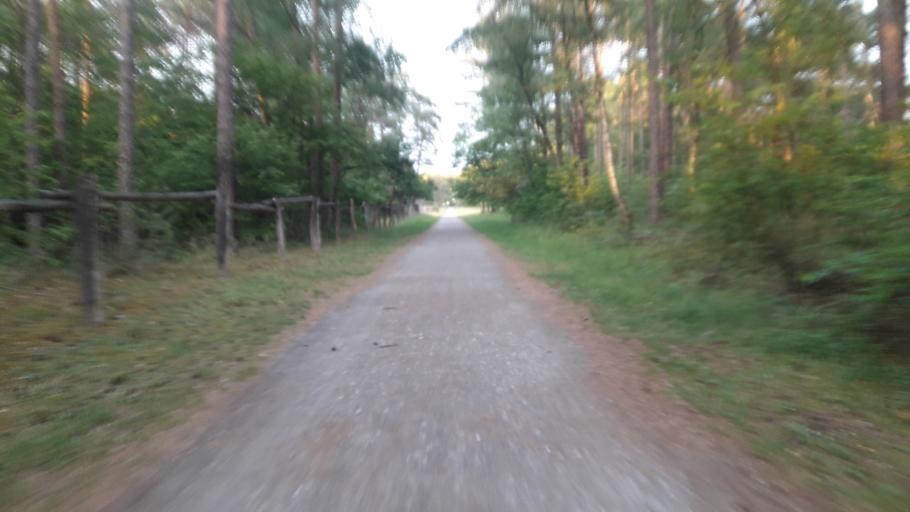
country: DE
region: North Rhine-Westphalia
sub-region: Regierungsbezirk Detmold
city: Hovelhof
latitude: 51.8560
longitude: 8.6938
